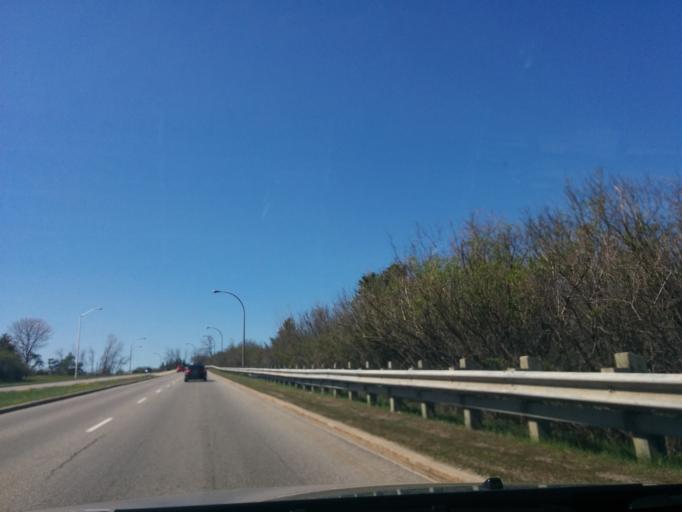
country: CA
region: Ontario
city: Ottawa
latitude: 45.3814
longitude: -75.6892
